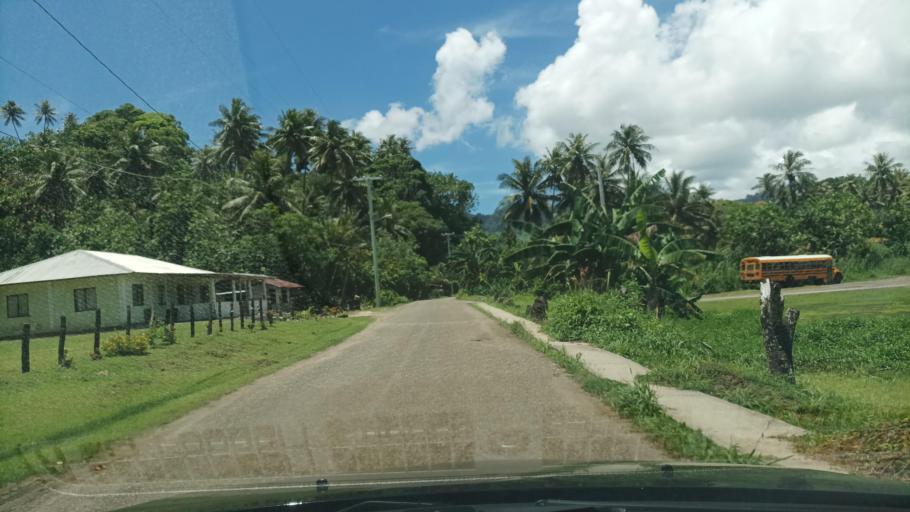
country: FM
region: Kosrae
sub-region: Lelu Municipality
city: Lelu
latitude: 5.3325
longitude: 163.0277
